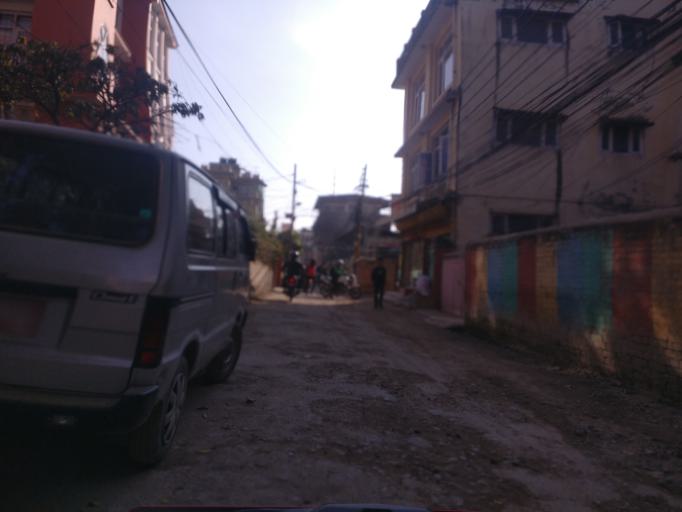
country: NP
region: Central Region
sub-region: Bagmati Zone
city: Patan
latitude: 27.6744
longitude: 85.3160
